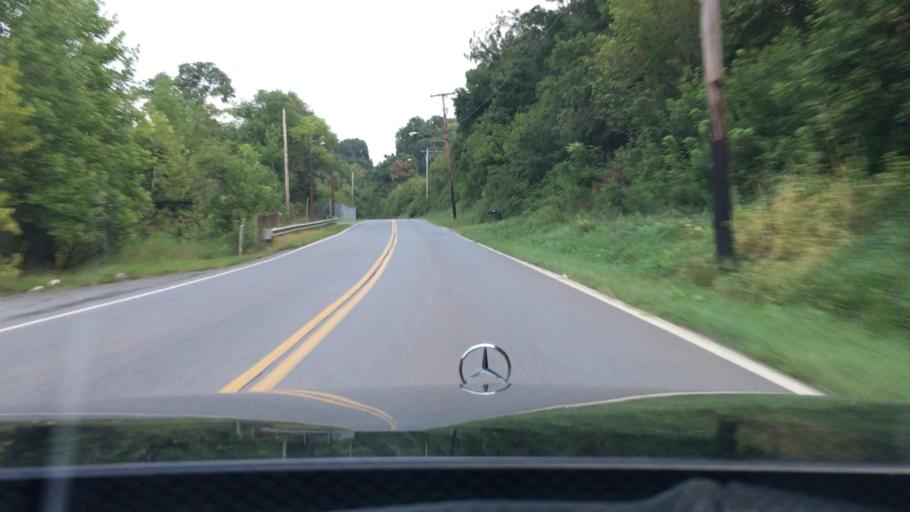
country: US
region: Virginia
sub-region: City of Lynchburg
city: Lynchburg
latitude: 37.3968
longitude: -79.1188
